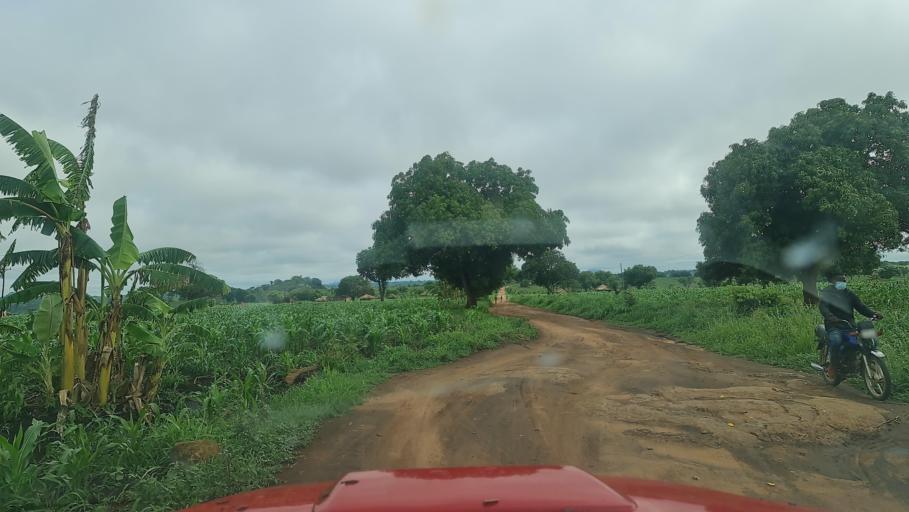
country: MW
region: Southern Region
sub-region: Nsanje District
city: Nsanje
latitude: -17.2105
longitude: 35.6786
